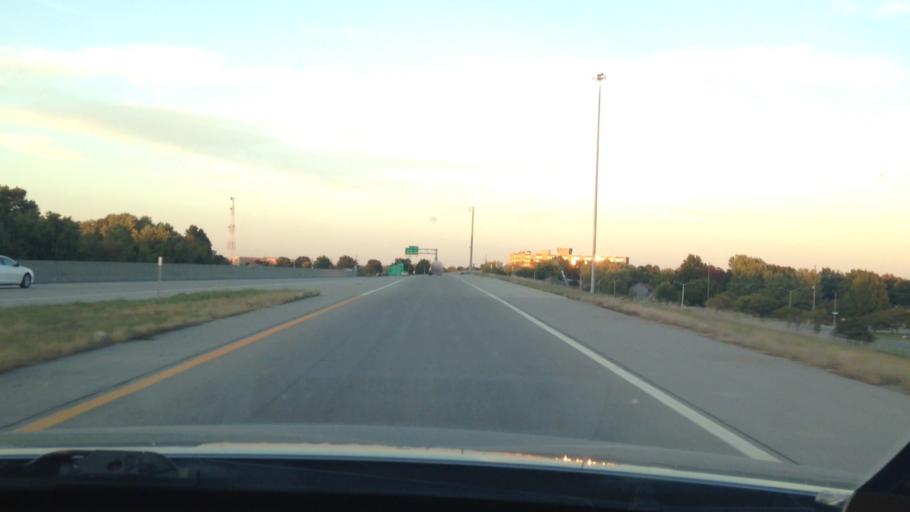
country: US
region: Kansas
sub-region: Johnson County
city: Olathe
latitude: 38.8705
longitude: -94.7966
